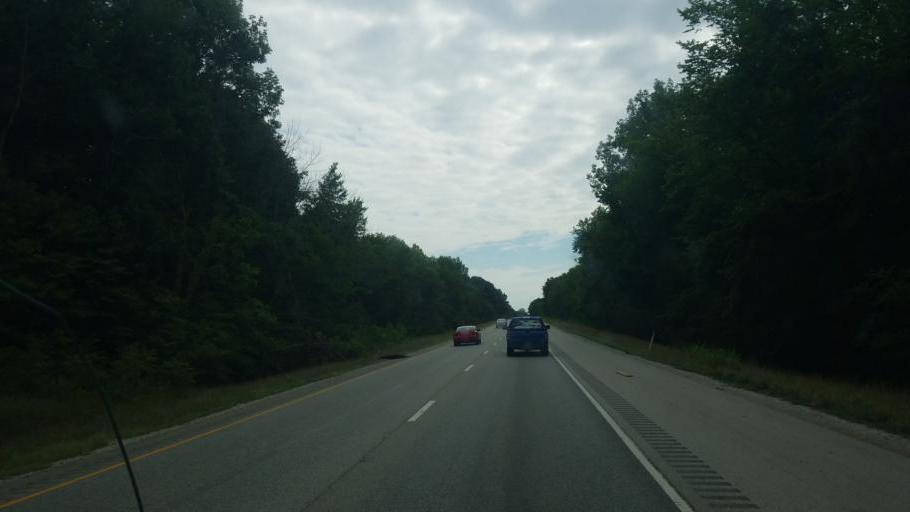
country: US
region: Indiana
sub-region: Vigo County
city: Seelyville
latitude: 39.4436
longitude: -87.2646
